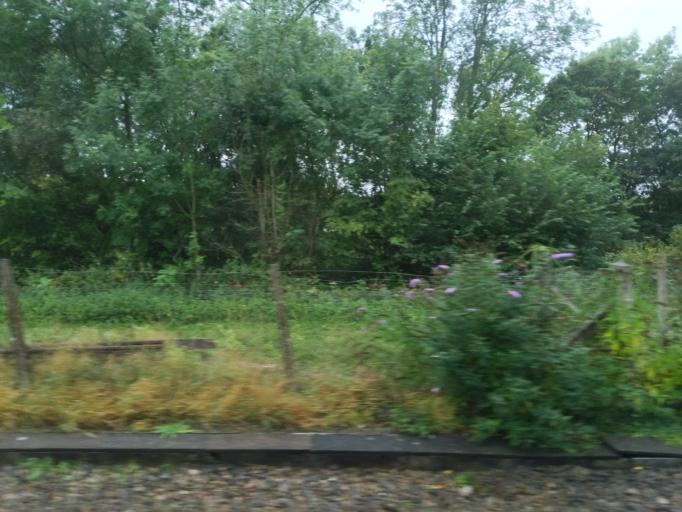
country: GB
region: England
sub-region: Kent
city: Tonbridge
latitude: 51.2139
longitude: 0.2302
